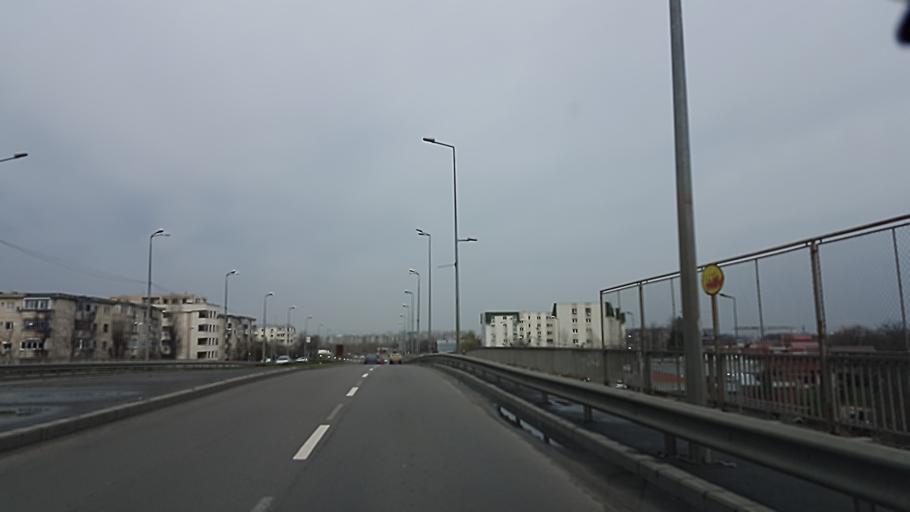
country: RO
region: Ilfov
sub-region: Comuna Fundeni-Dobroesti
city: Fundeni
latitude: 44.4496
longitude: 26.1533
